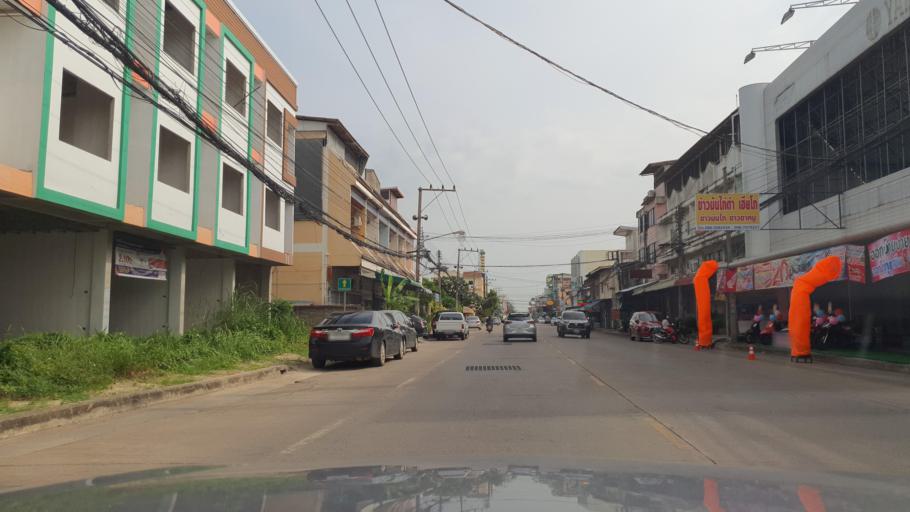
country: TH
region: Phitsanulok
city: Phitsanulok
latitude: 16.8307
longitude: 100.2655
